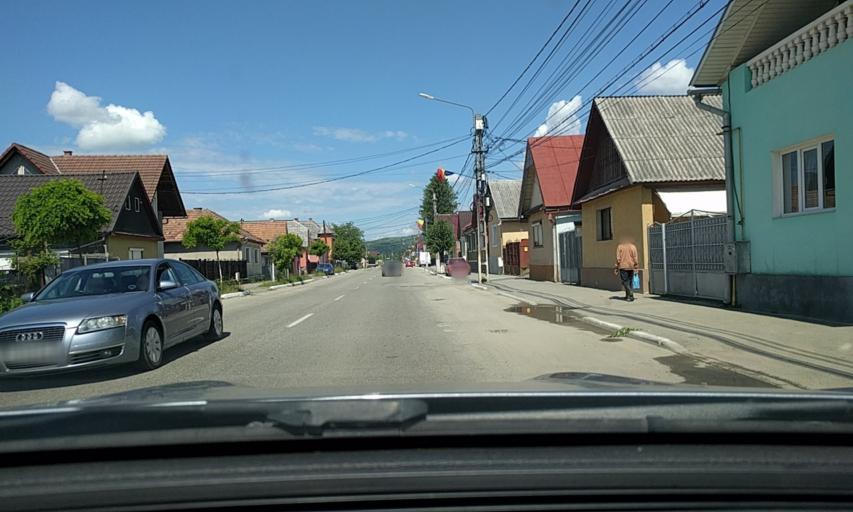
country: RO
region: Bistrita-Nasaud
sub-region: Oras Nasaud
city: Nasaud
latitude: 47.2911
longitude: 24.3895
